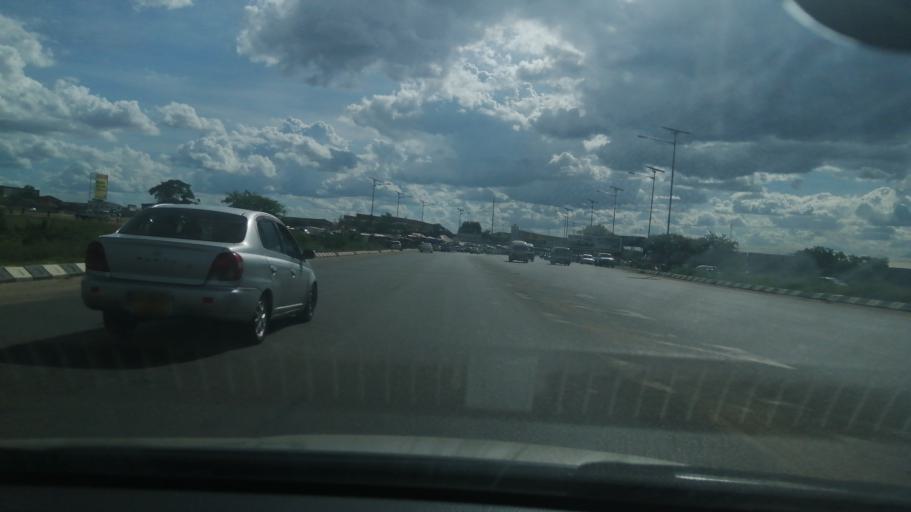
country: ZW
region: Harare
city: Harare
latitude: -17.8514
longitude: 31.0562
